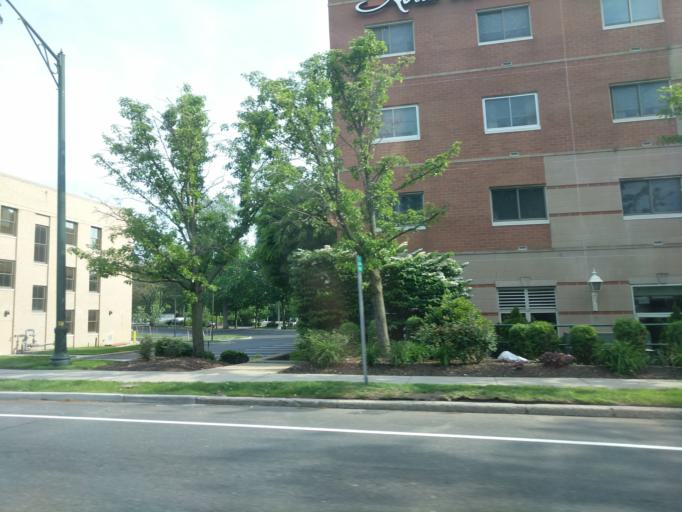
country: US
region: New York
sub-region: Nassau County
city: Lynbrook
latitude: 40.6561
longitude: -73.6792
